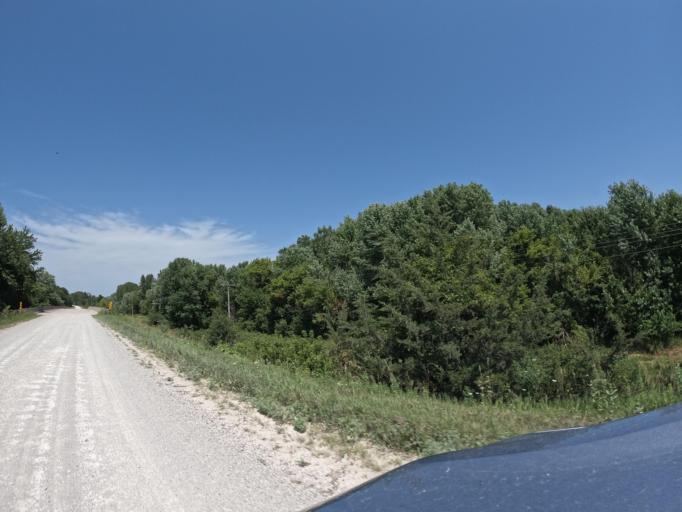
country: US
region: Iowa
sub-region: Henry County
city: Mount Pleasant
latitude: 40.9693
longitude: -91.6798
